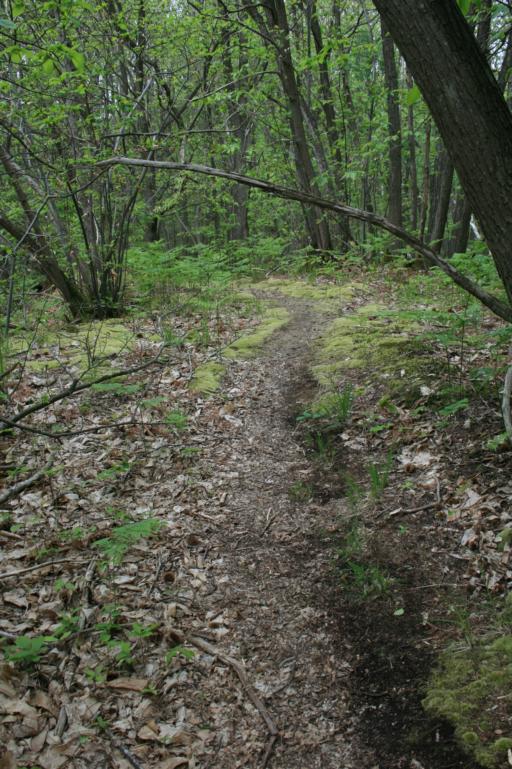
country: FR
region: Ile-de-France
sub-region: Departement des Yvelines
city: Vaux-sur-Seine
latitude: 49.0068
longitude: 1.9906
